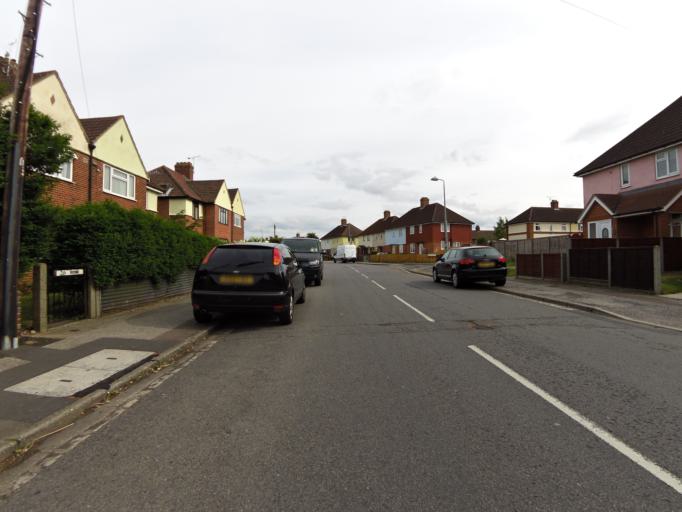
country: GB
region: England
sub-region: Suffolk
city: Ipswich
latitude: 52.0337
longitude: 1.1828
